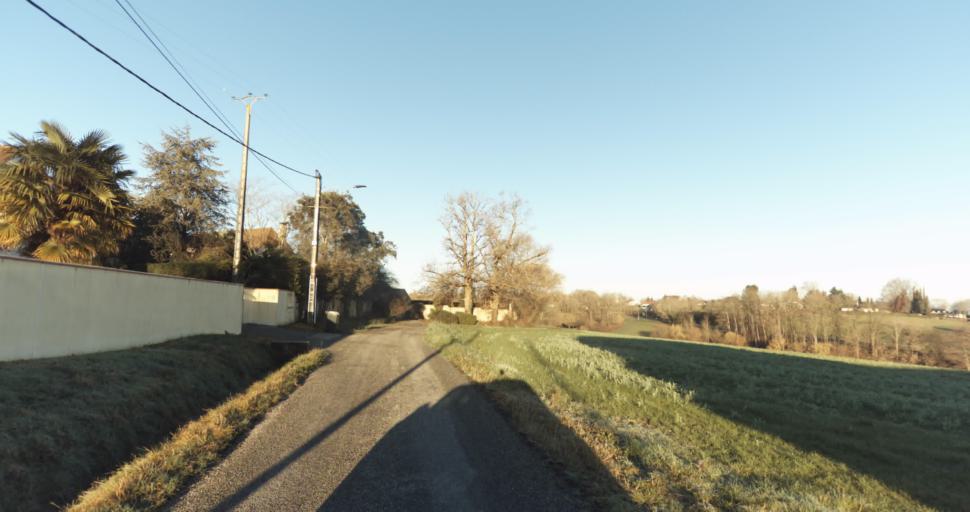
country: FR
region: Aquitaine
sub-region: Departement des Pyrenees-Atlantiques
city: Morlaas
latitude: 43.3348
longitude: -0.2696
